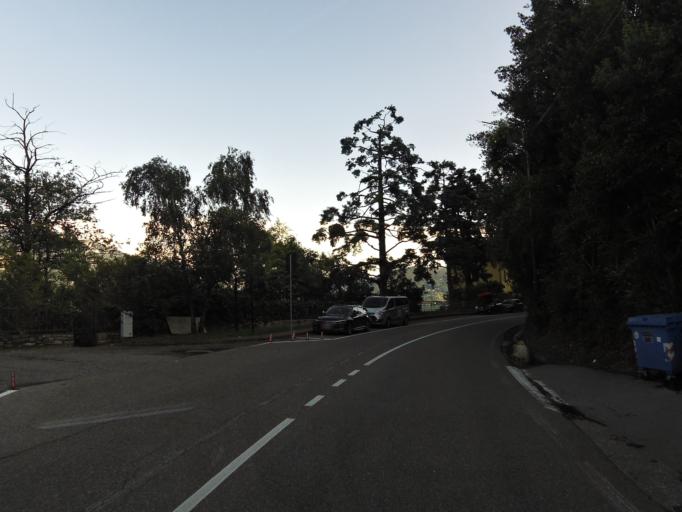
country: IT
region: Lombardy
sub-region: Provincia di Como
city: Menaggio
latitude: 46.0150
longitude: 9.2368
